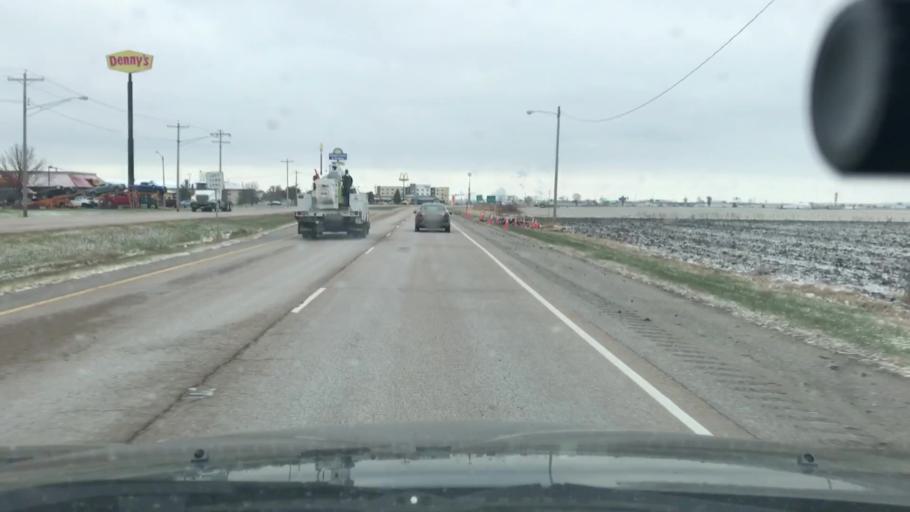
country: US
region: Illinois
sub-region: Madison County
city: Pontoon Beach
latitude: 38.7454
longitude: -90.0712
